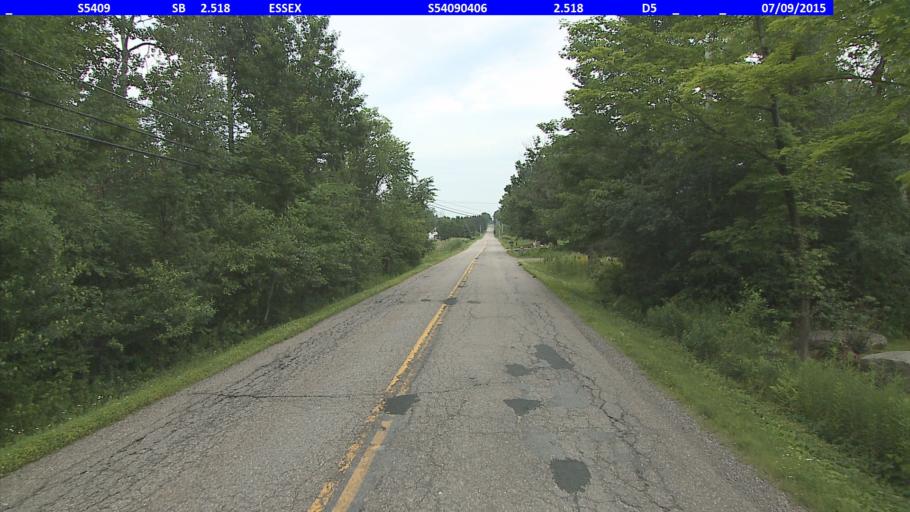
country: US
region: Vermont
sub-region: Chittenden County
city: Essex Junction
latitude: 44.5450
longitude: -73.0718
